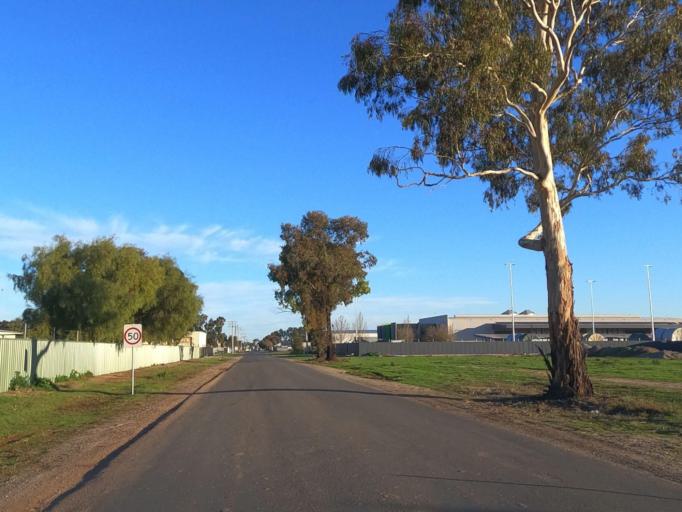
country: AU
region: Victoria
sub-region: Swan Hill
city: Swan Hill
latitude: -35.3255
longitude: 143.5354
